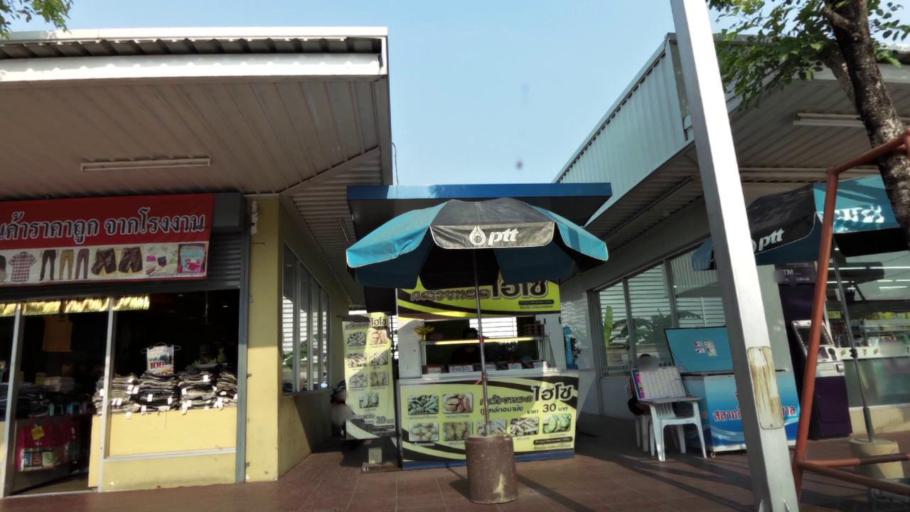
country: TH
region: Phra Nakhon Si Ayutthaya
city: Phra Nakhon Si Ayutthaya
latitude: 14.3270
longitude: 100.6276
